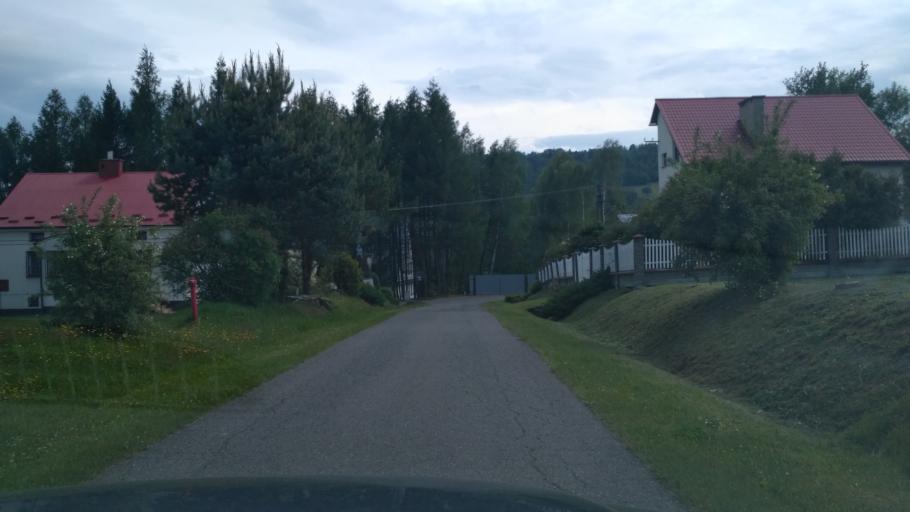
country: PL
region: Subcarpathian Voivodeship
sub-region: Powiat strzyzowski
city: Frysztak
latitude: 49.8750
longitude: 21.5815
